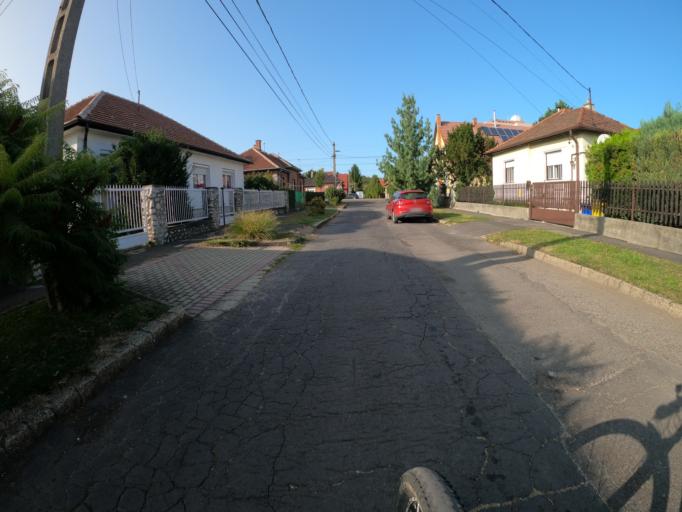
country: HU
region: Borsod-Abauj-Zemplen
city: Sajobabony
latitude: 48.0994
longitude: 20.7020
